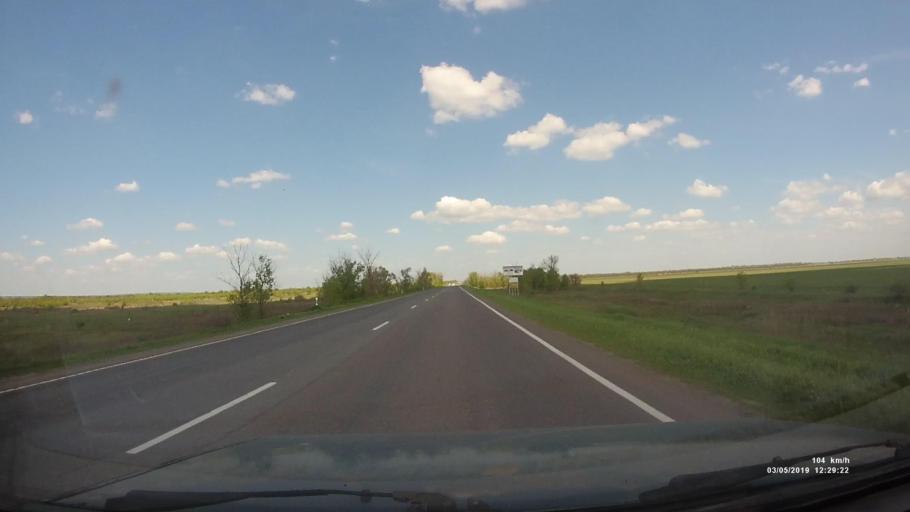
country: RU
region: Rostov
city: Semikarakorsk
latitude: 47.4867
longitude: 40.7352
